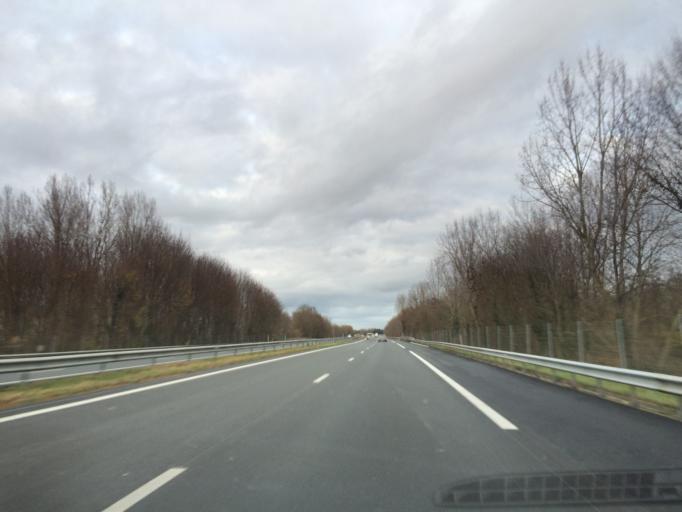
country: FR
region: Poitou-Charentes
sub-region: Departement des Deux-Sevres
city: Aiffres
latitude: 46.2773
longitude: -0.4008
